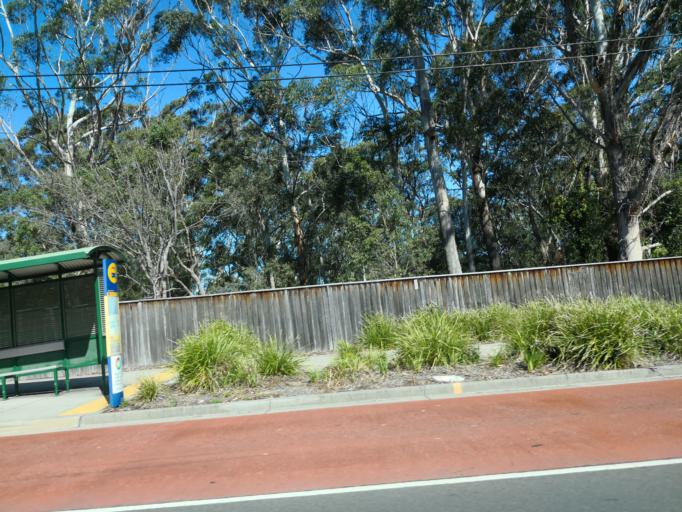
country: AU
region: New South Wales
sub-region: Gosford Shire
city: Erina
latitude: -33.4260
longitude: 151.3993
